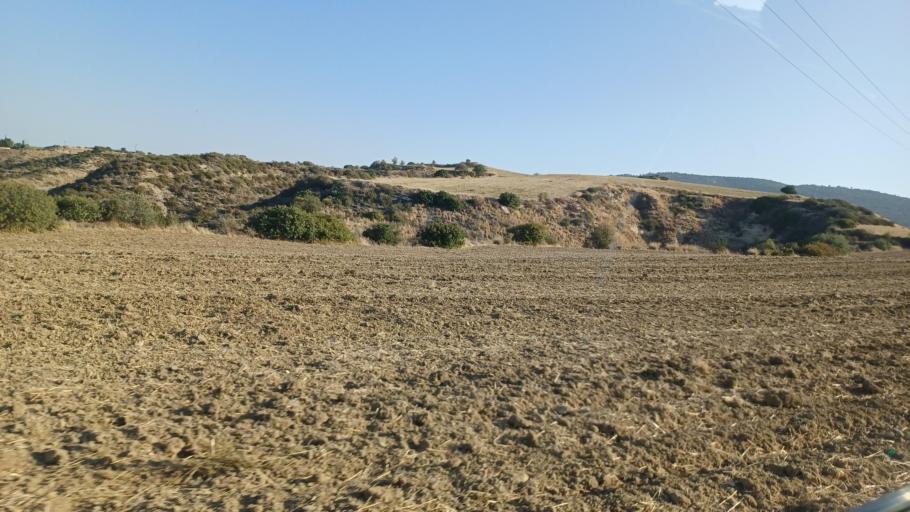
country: CY
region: Pafos
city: Polis
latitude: 34.9994
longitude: 32.4570
